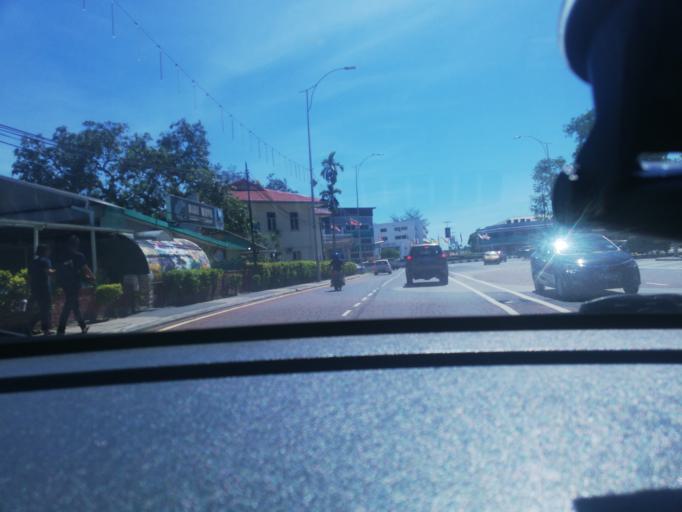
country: MY
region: Labuan
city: Victoria
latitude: 5.2767
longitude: 115.2442
